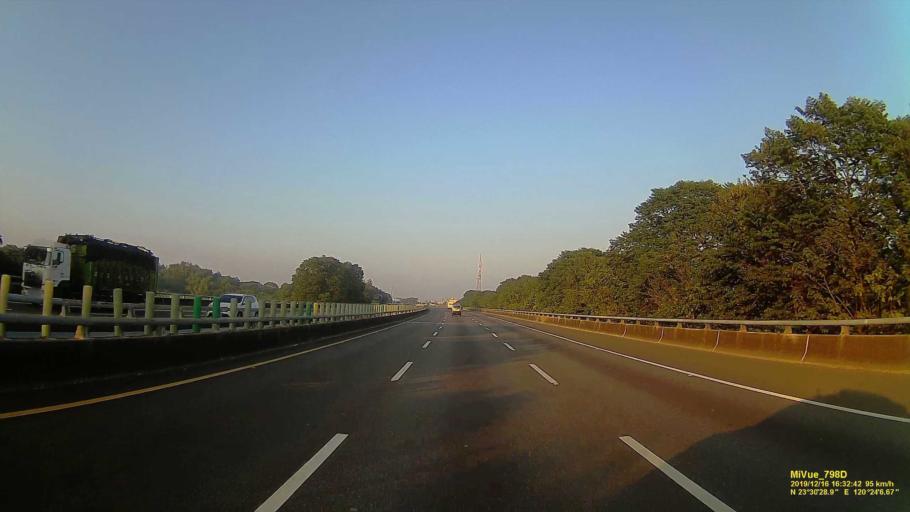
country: TW
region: Taiwan
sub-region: Chiayi
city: Jiayi Shi
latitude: 23.5088
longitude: 120.4022
